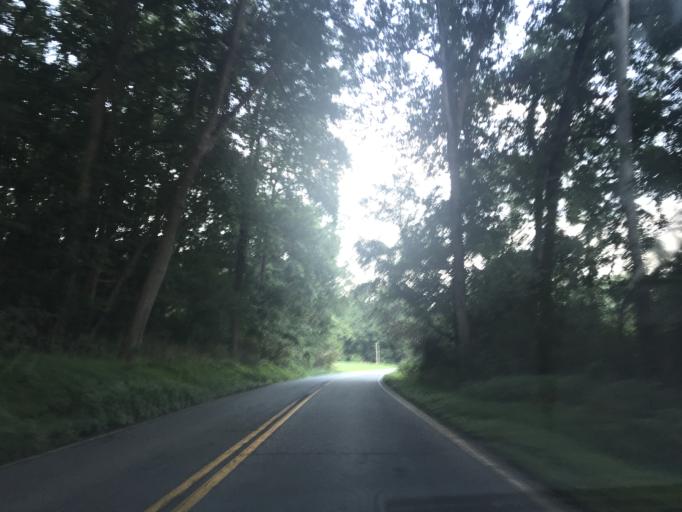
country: US
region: Maryland
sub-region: Cecil County
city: Rising Sun
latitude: 39.6637
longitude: -76.1618
